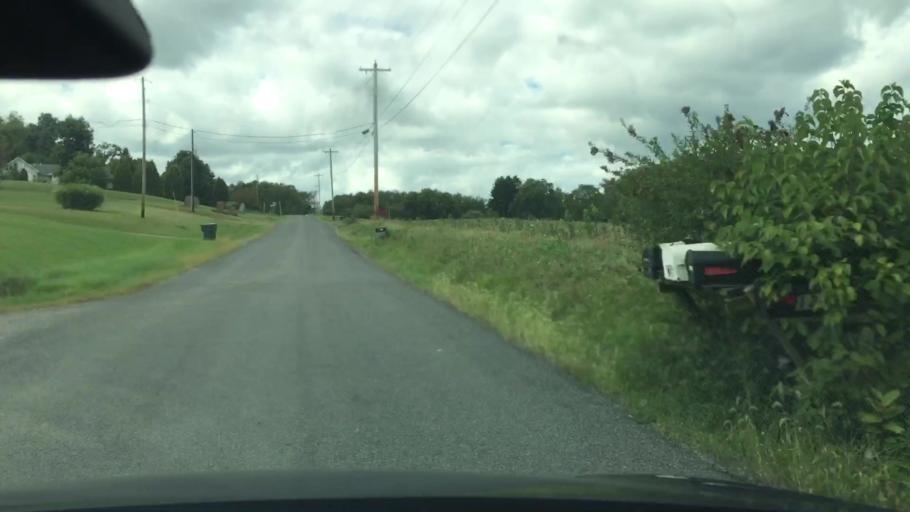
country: US
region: Pennsylvania
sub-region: Butler County
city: Saxonburg
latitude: 40.7307
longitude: -79.8745
